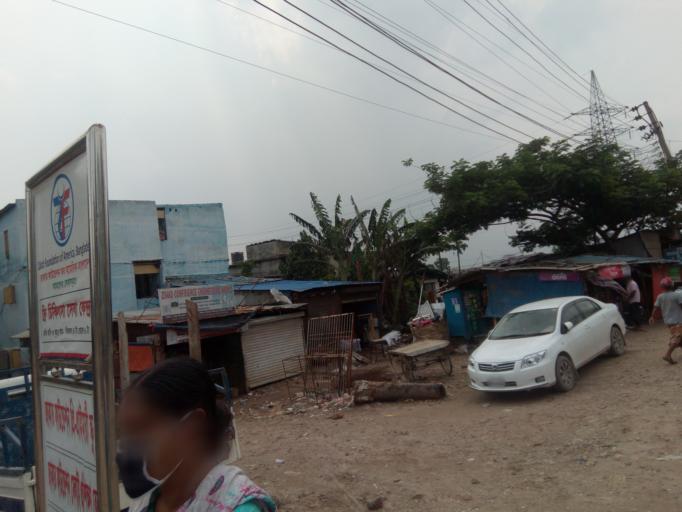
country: BD
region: Dhaka
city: Azimpur
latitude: 23.7435
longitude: 90.3598
